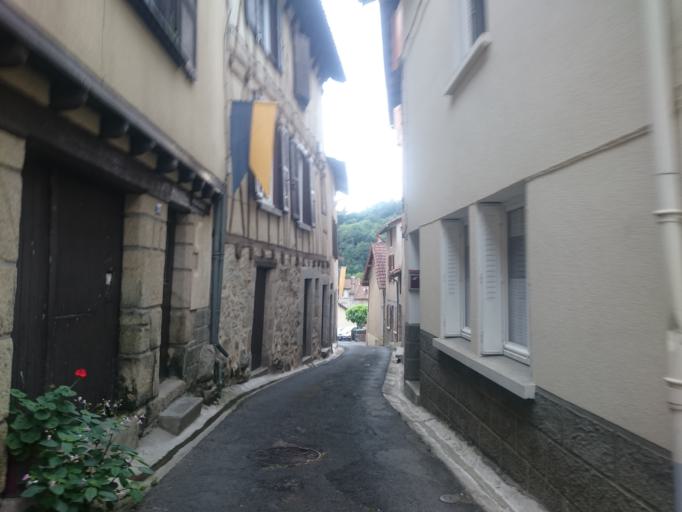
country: FR
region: Auvergne
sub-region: Departement du Cantal
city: Laroquebrou
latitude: 44.9695
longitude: 2.1899
